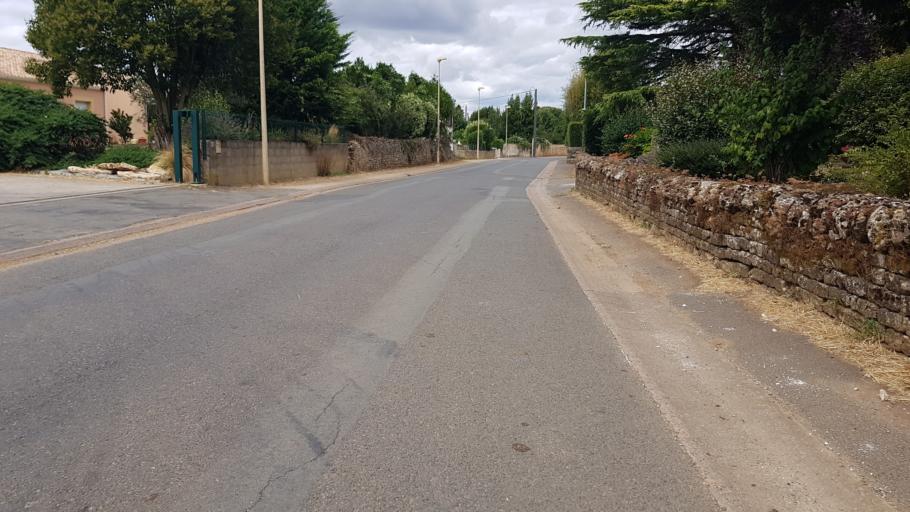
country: FR
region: Poitou-Charentes
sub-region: Departement des Deux-Sevres
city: Vouille
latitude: 46.3064
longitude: -0.3414
